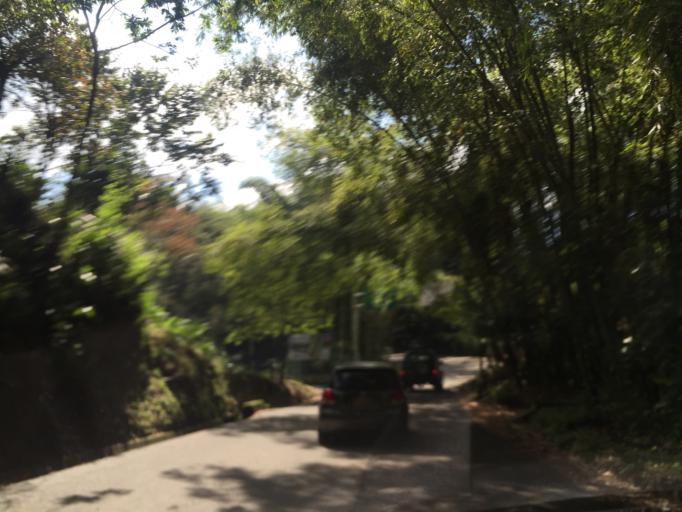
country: CO
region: Valle del Cauca
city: Alcala
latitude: 4.6899
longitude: -75.7784
